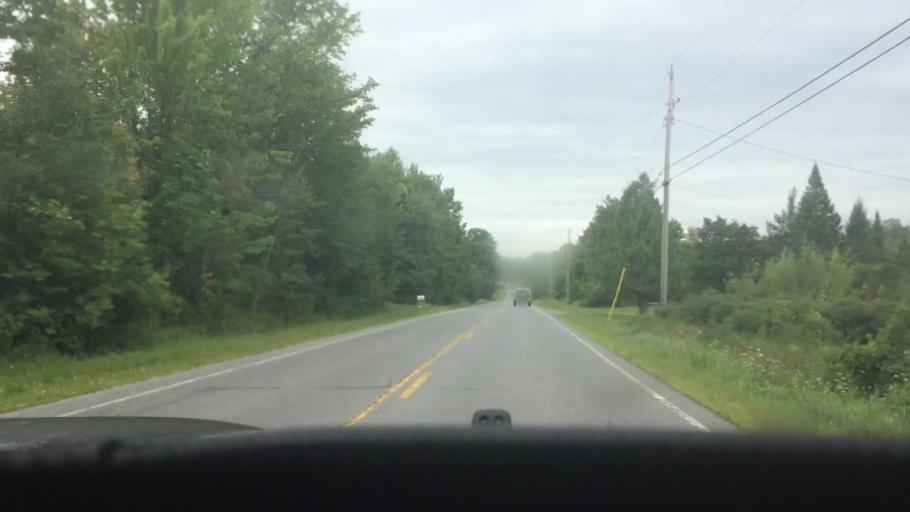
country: US
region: New York
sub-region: St. Lawrence County
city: Canton
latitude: 44.5047
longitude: -75.2135
